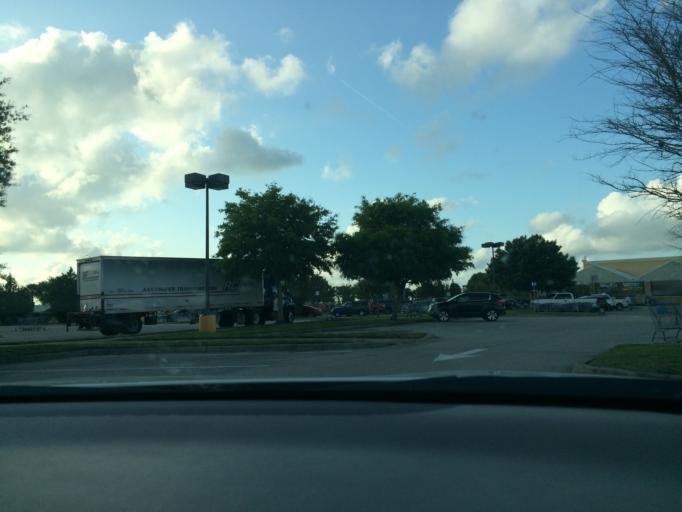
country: US
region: Florida
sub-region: Manatee County
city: Ellenton
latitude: 27.4943
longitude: -82.4833
